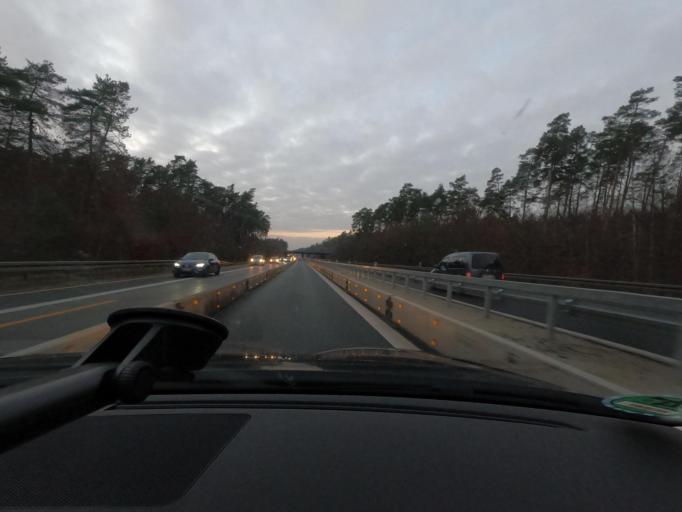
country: DE
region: Bavaria
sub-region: Upper Franconia
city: Strullendorf
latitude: 49.8572
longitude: 10.9763
